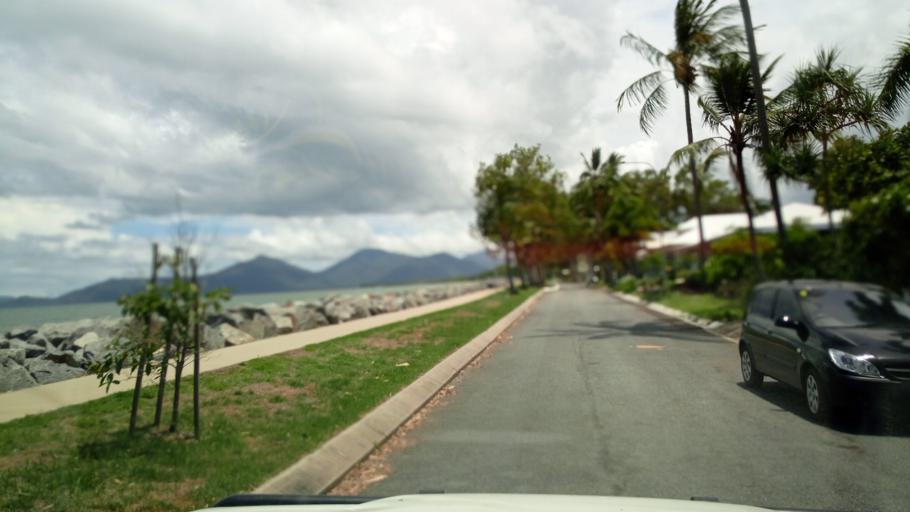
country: AU
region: Queensland
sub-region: Cairns
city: Yorkeys Knob
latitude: -16.8471
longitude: 145.7464
